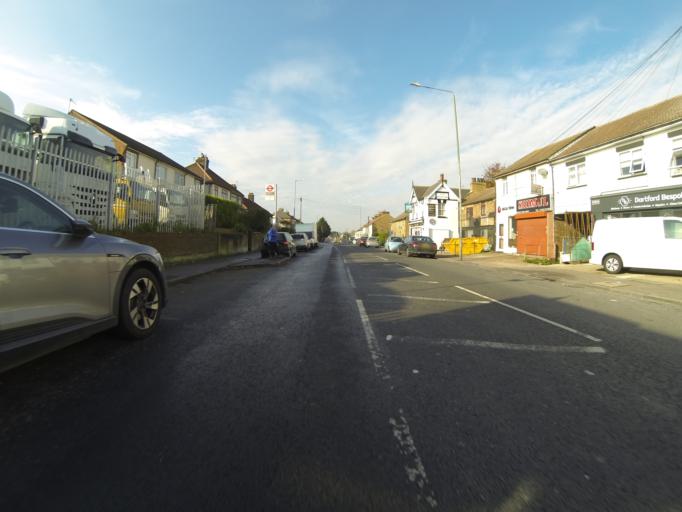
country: GB
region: England
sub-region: Kent
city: Dartford
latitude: 51.4474
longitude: 0.1989
